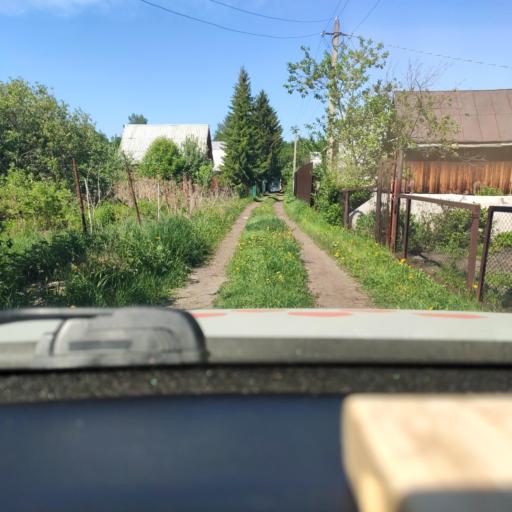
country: RU
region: Bashkortostan
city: Kabakovo
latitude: 54.6634
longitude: 56.1018
